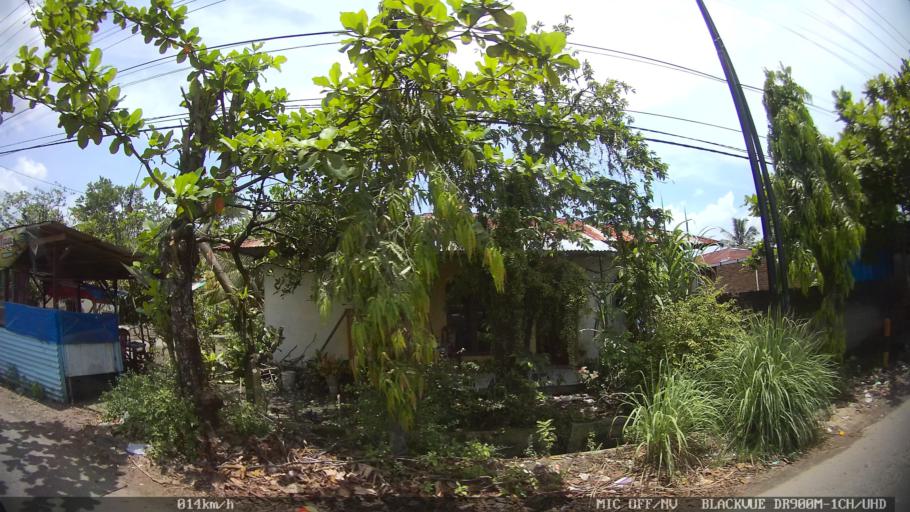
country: ID
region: North Sumatra
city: Binjai
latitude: 3.6276
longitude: 98.5186
